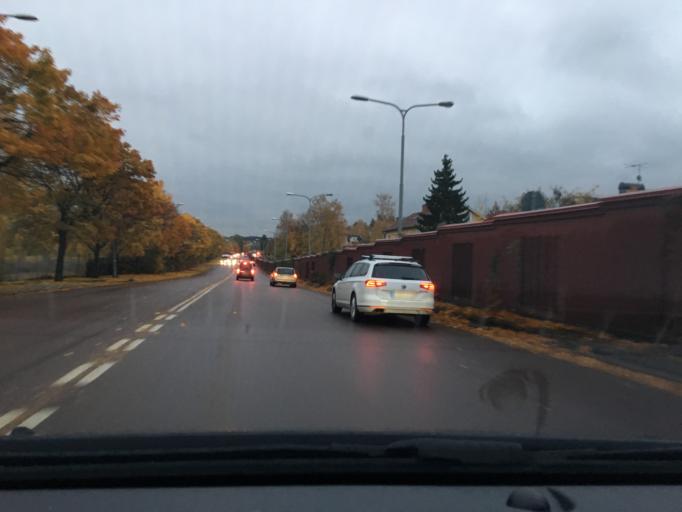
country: SE
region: Stockholm
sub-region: Stockholms Kommun
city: Kista
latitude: 59.3766
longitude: 17.9106
